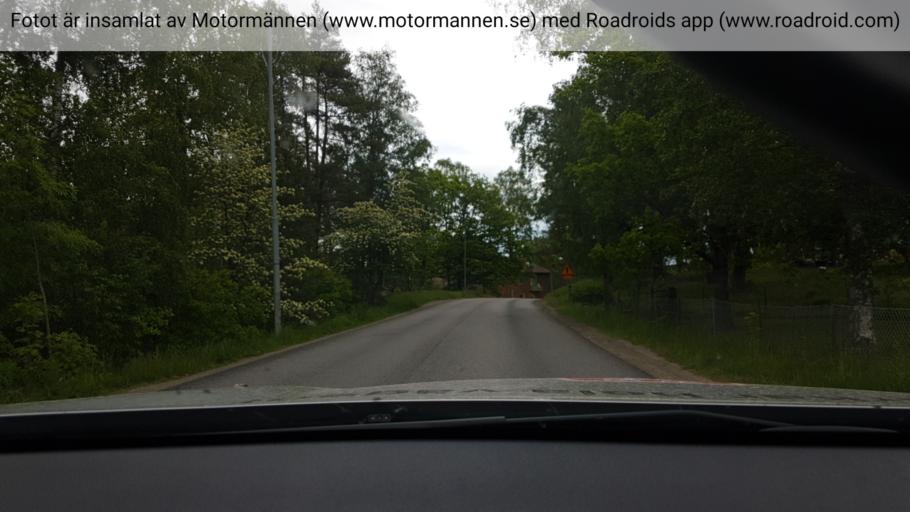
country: SE
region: Stockholm
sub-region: Nynashamns Kommun
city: Osmo
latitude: 58.9824
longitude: 17.9000
